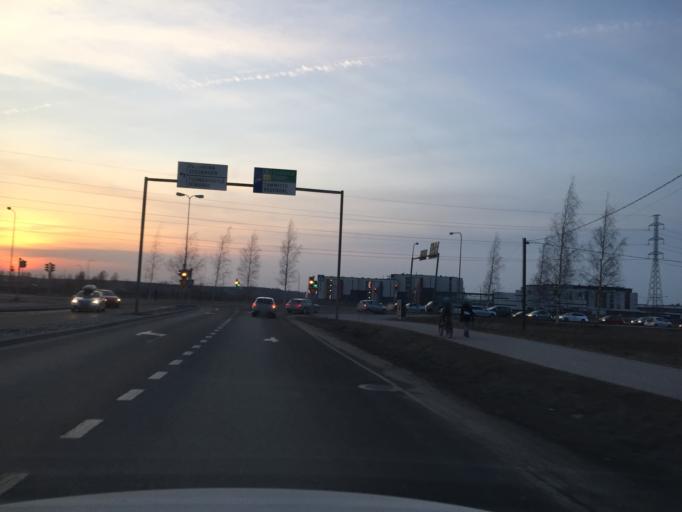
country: FI
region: Uusimaa
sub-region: Helsinki
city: Vantaa
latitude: 60.2654
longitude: 24.9741
